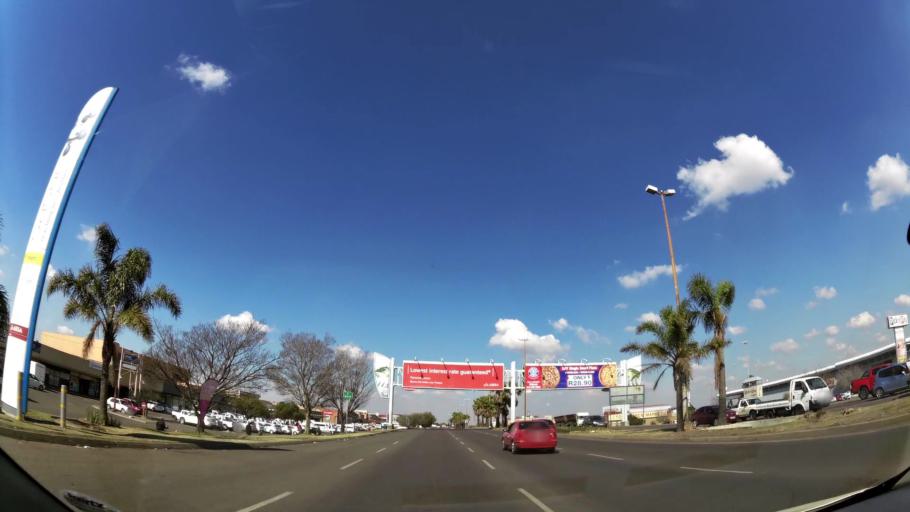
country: ZA
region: Mpumalanga
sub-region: Nkangala District Municipality
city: Witbank
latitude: -25.8993
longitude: 29.2324
